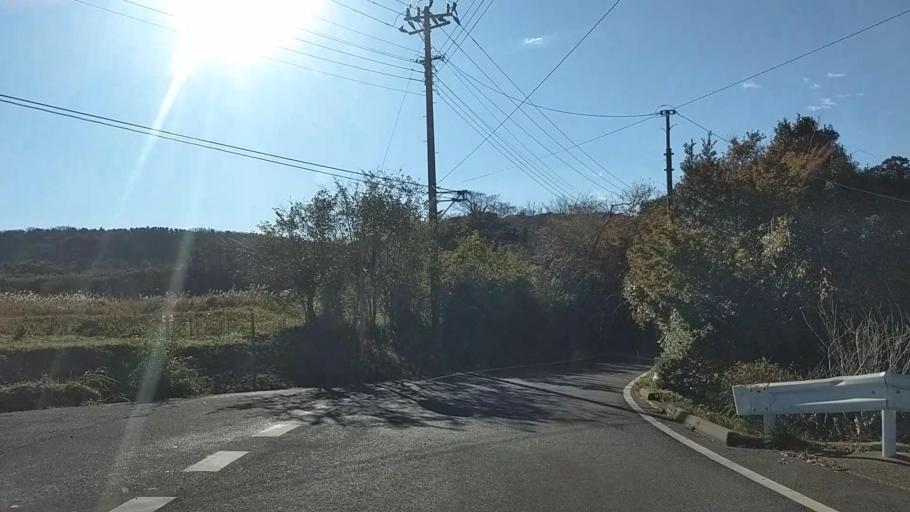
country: JP
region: Chiba
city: Futtsu
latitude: 35.2325
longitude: 139.8770
